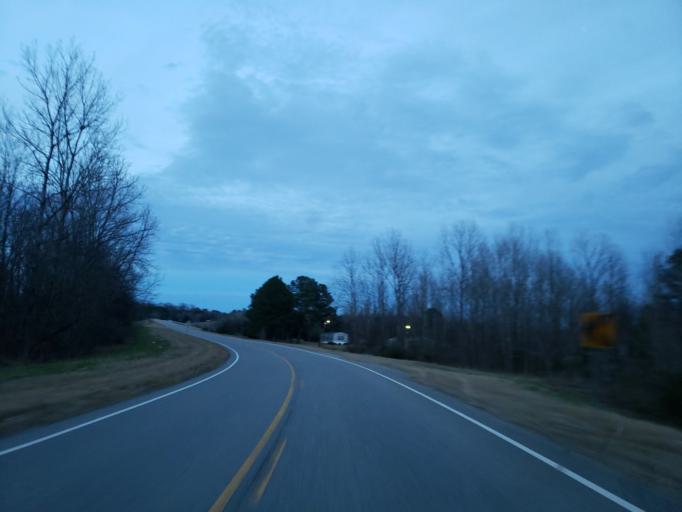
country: US
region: Alabama
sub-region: Greene County
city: Eutaw
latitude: 32.8549
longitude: -88.1022
